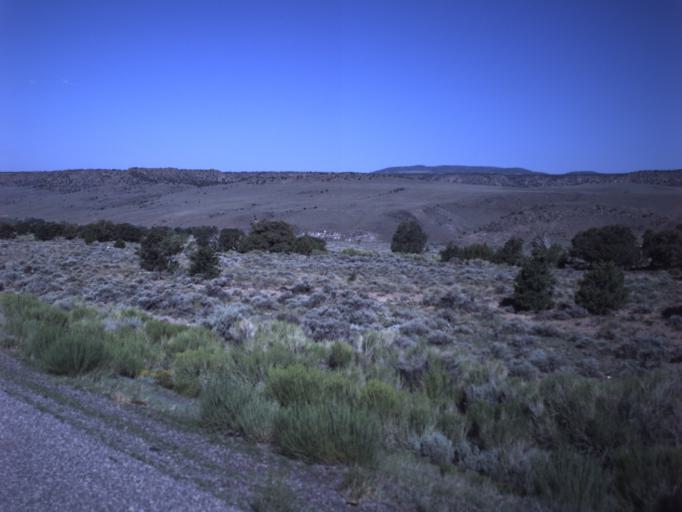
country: US
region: Utah
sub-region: Wayne County
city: Loa
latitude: 38.4781
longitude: -111.5670
